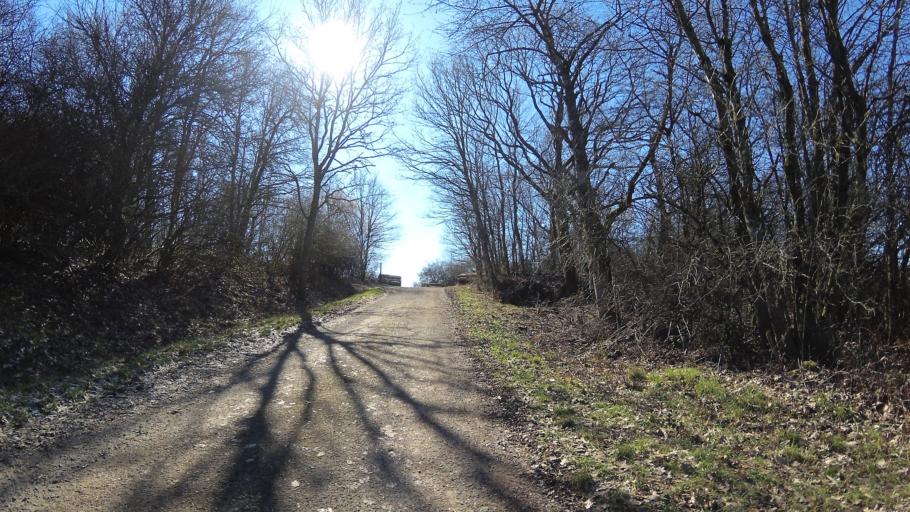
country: DE
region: Rheinland-Pfalz
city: Breitenbach
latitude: 49.4540
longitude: 7.2472
